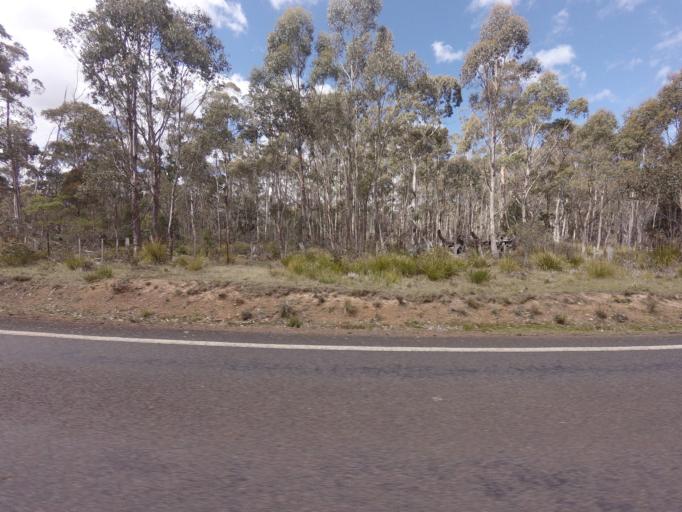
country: AU
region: Tasmania
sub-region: Northern Midlands
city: Evandale
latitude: -42.0152
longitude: 147.7342
